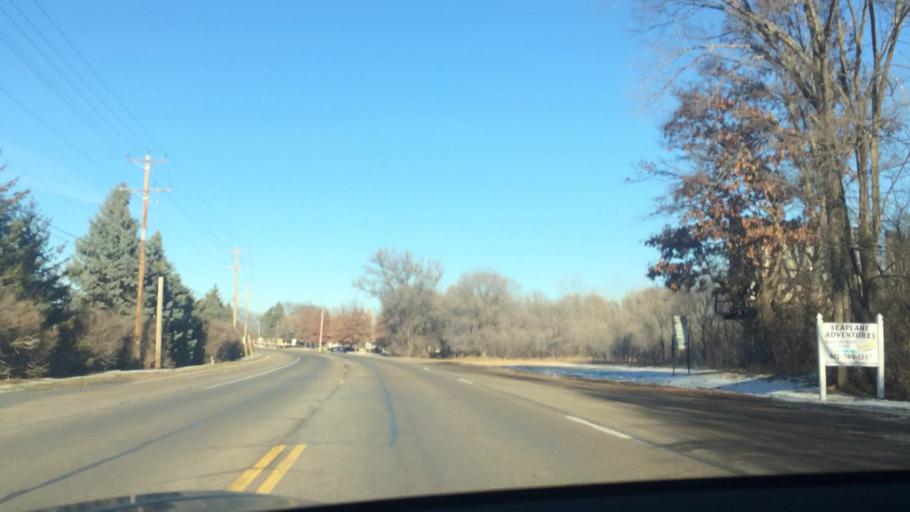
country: US
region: Minnesota
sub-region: Anoka County
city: Circle Pines
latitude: 45.1603
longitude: -93.1251
